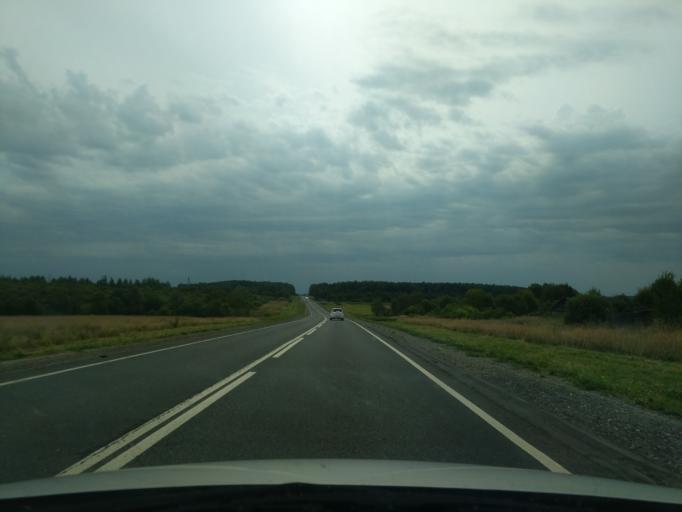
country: RU
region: Kostroma
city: Manturovo
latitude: 58.3119
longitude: 44.7214
